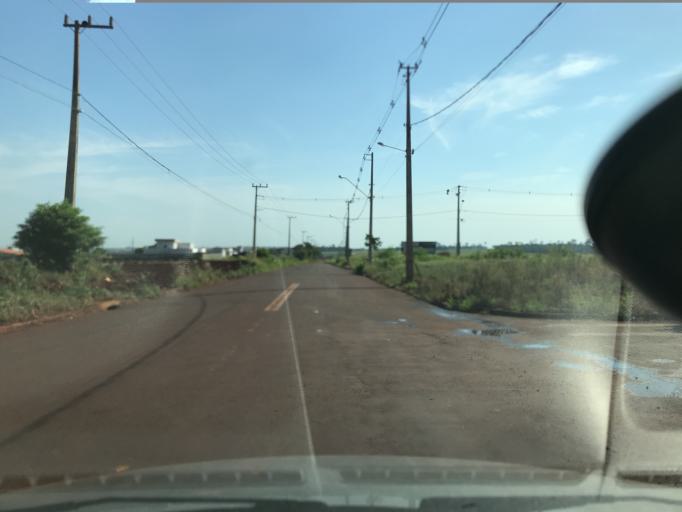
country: BR
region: Parana
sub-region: Palotina
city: Palotina
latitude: -24.2934
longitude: -53.8289
